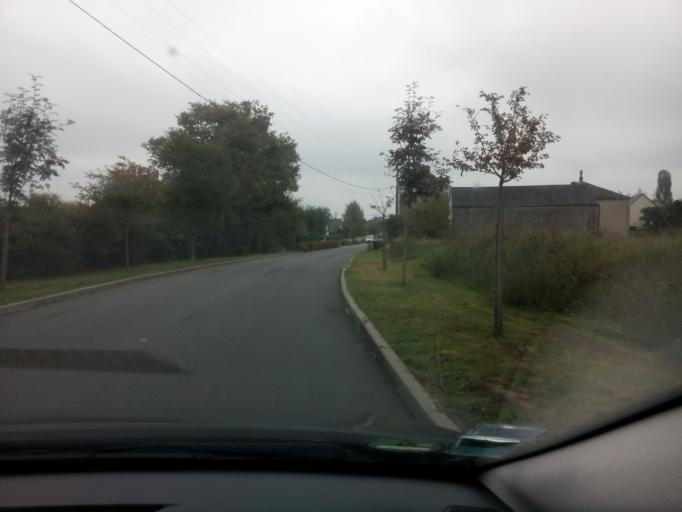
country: FR
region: Pays de la Loire
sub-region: Departement de Maine-et-Loire
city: Soulaire-et-Bourg
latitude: 47.6154
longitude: -0.5657
